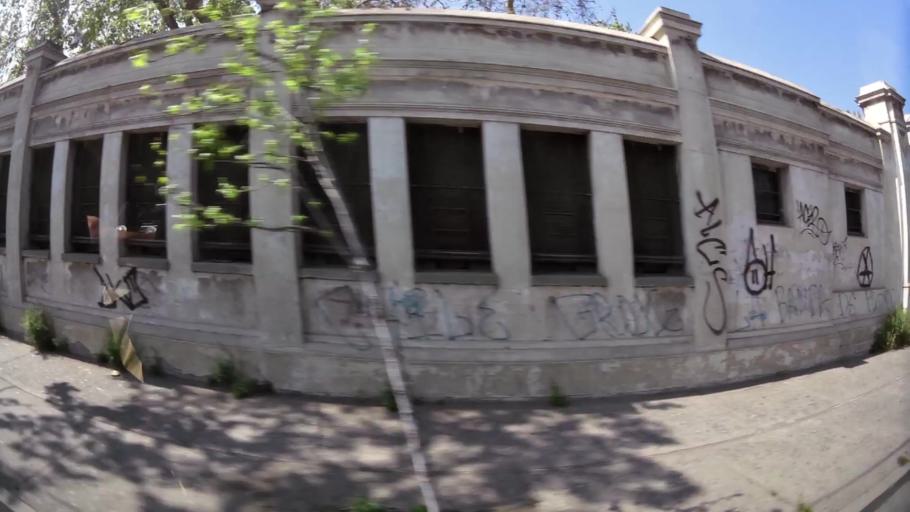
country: CL
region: Santiago Metropolitan
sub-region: Provincia de Santiago
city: Santiago
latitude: -33.4608
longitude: -70.6717
